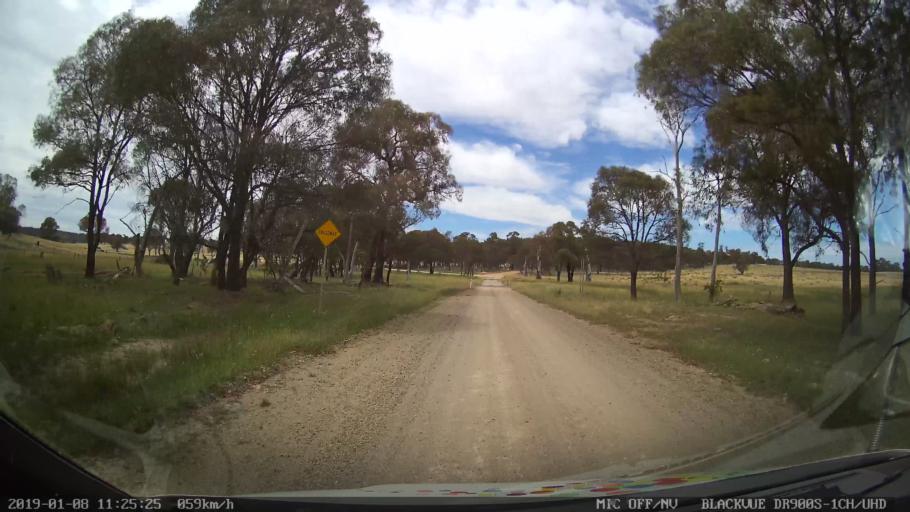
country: AU
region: New South Wales
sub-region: Guyra
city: Guyra
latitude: -30.2732
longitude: 151.5610
